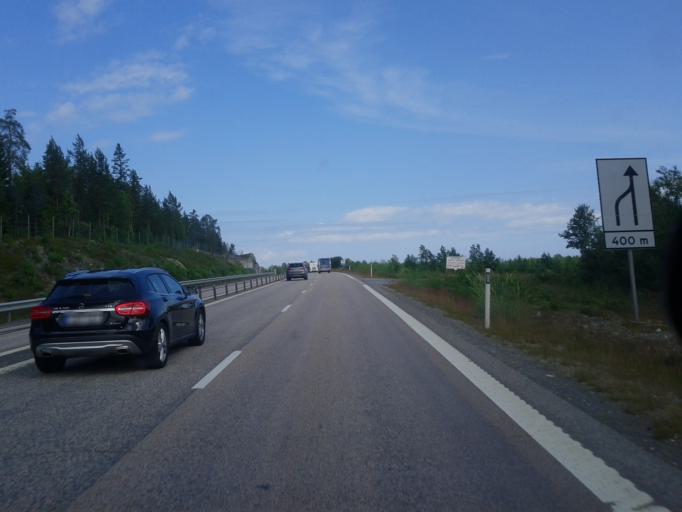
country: SE
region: Vaesternorrland
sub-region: OErnskoeldsviks Kommun
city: Husum
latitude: 63.3654
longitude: 19.1833
